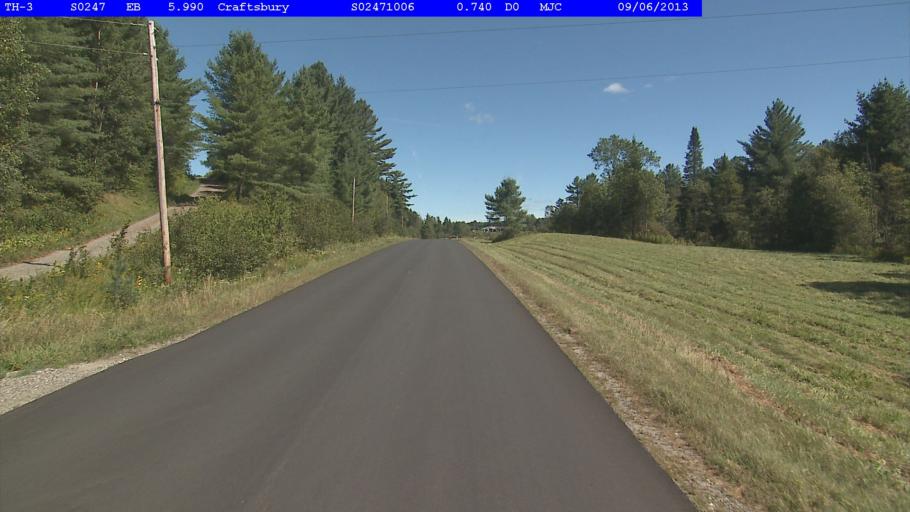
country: US
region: Vermont
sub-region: Caledonia County
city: Hardwick
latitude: 44.6276
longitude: -72.4340
